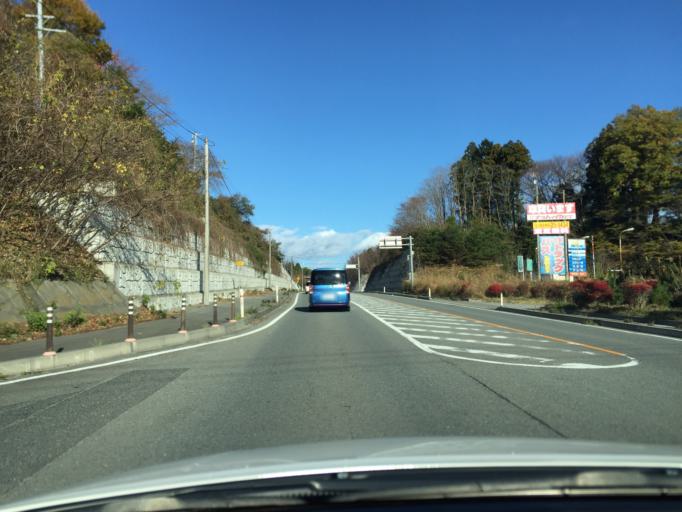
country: JP
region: Fukushima
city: Namie
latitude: 37.2837
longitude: 140.9919
